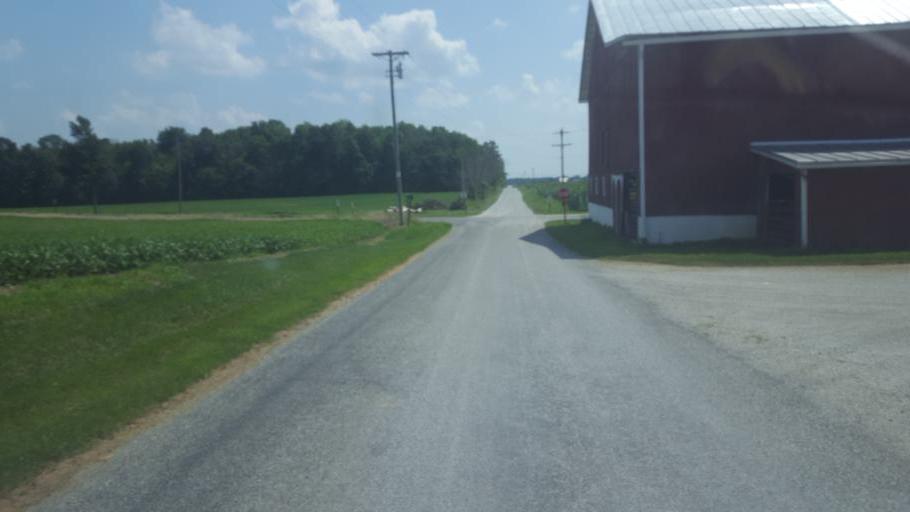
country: US
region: Ohio
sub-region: Richland County
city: Lexington
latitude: 40.6239
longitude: -82.6902
